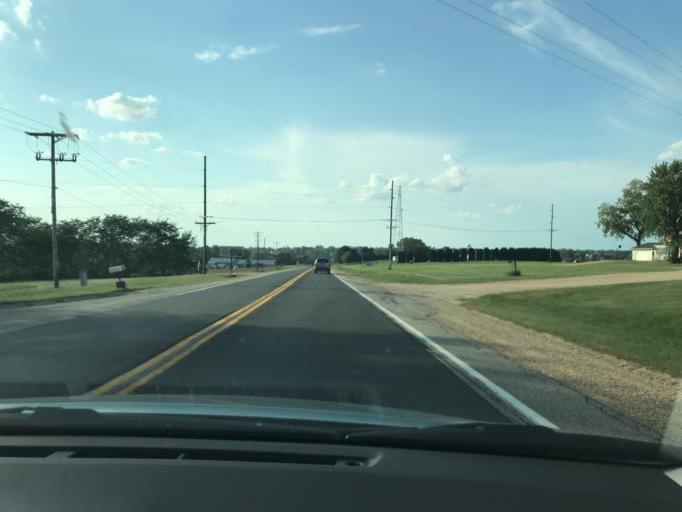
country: US
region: Wisconsin
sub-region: Grant County
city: Platteville
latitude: 42.7191
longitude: -90.4651
